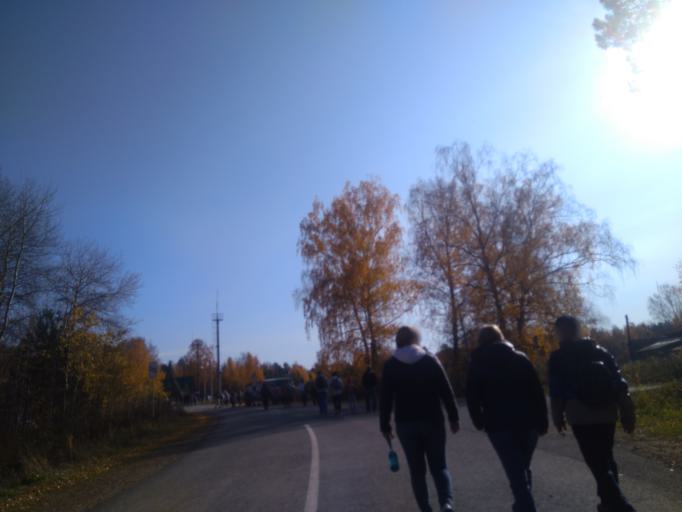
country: RU
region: Sverdlovsk
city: Mikhaylovsk
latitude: 56.5252
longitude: 59.2273
